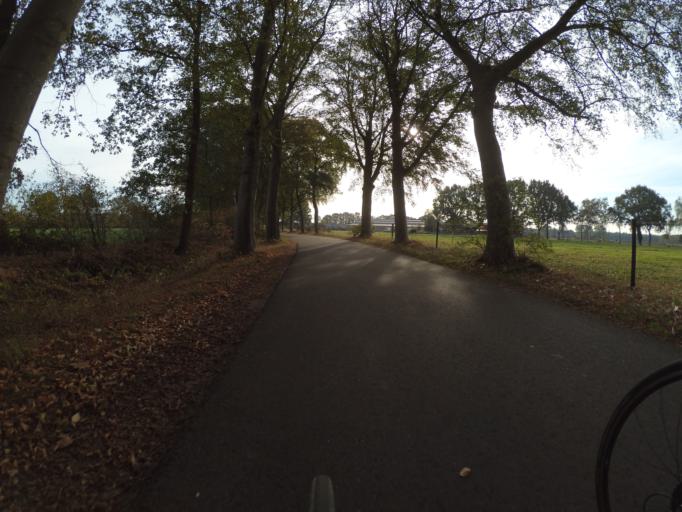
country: NL
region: Gelderland
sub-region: Gemeente Lochem
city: Harfsen
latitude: 52.2819
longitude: 6.3104
